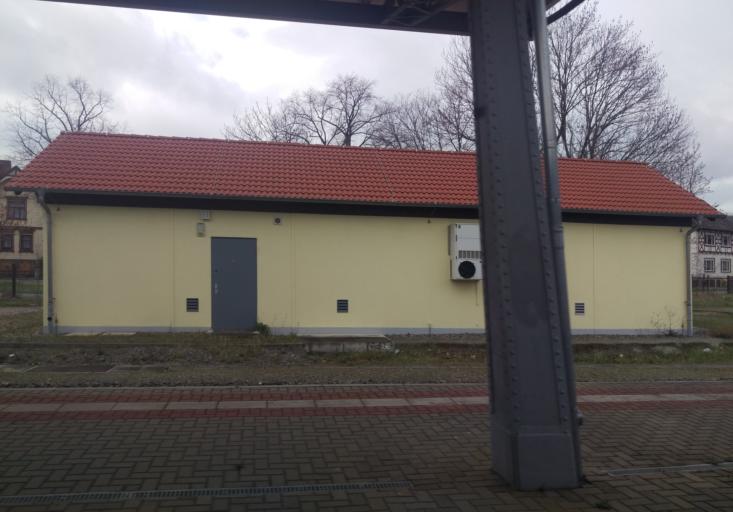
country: DE
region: Saxony-Anhalt
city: Ilsenburg
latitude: 51.8697
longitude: 10.6827
